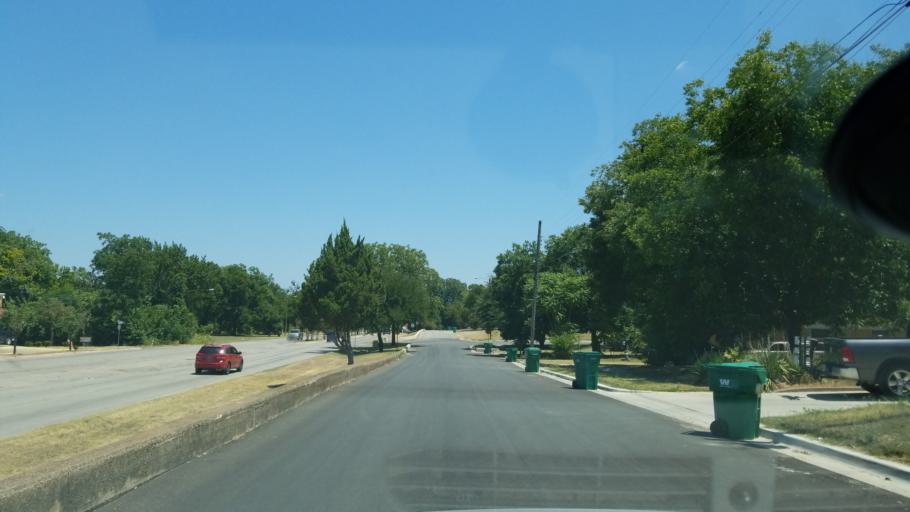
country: US
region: Texas
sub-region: Dallas County
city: Cockrell Hill
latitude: 32.7387
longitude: -96.8851
